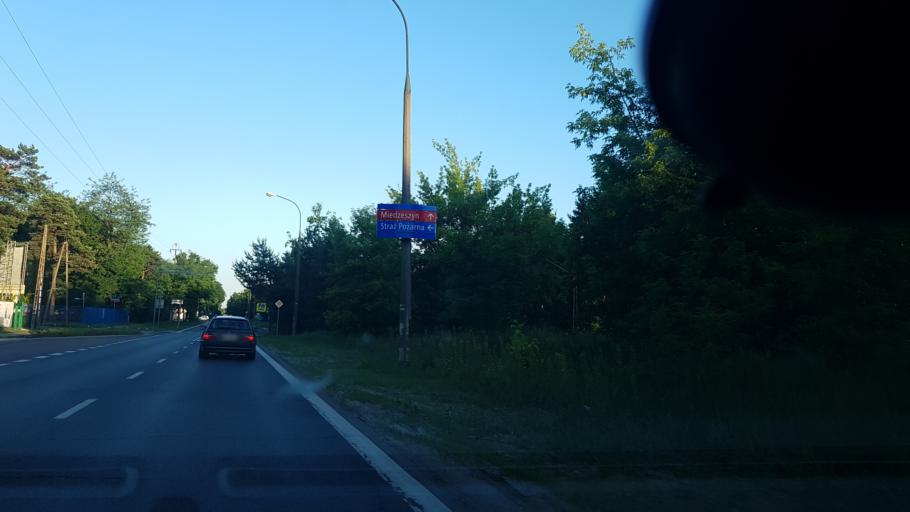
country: PL
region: Masovian Voivodeship
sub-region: Warszawa
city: Wawer
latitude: 52.1821
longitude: 21.1913
